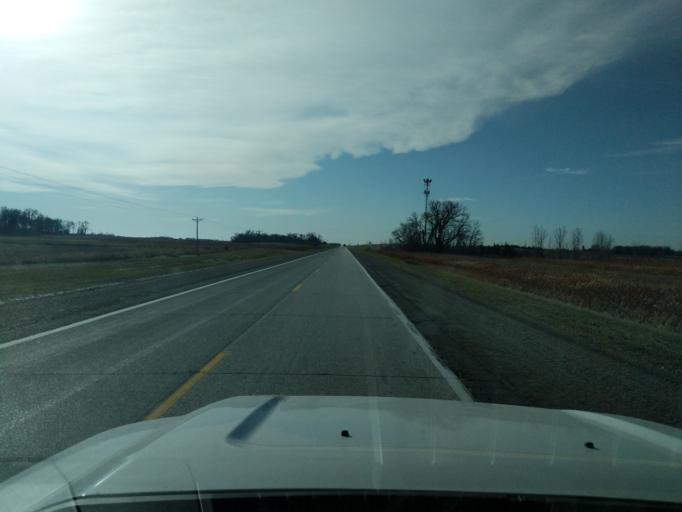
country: US
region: Minnesota
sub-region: Yellow Medicine County
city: Granite Falls
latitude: 44.8388
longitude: -95.4836
